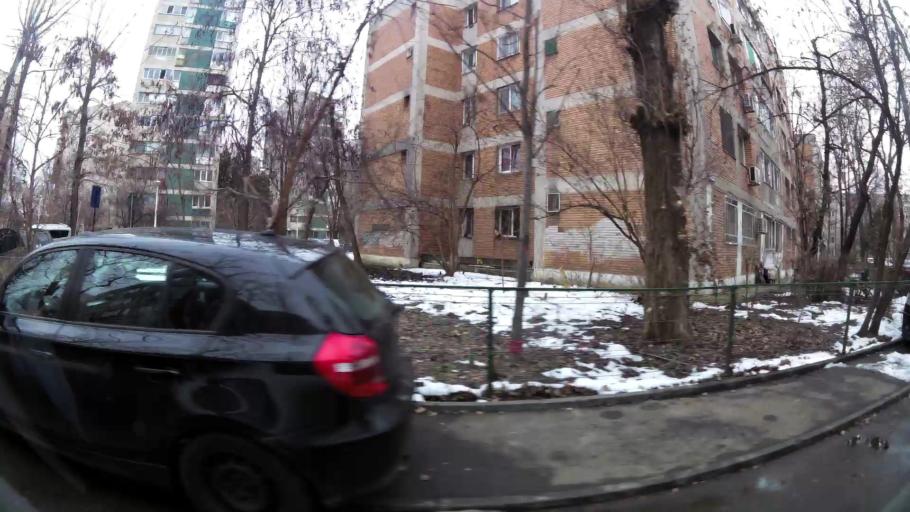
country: RO
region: Ilfov
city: Dobroesti
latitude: 44.4283
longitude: 26.1739
